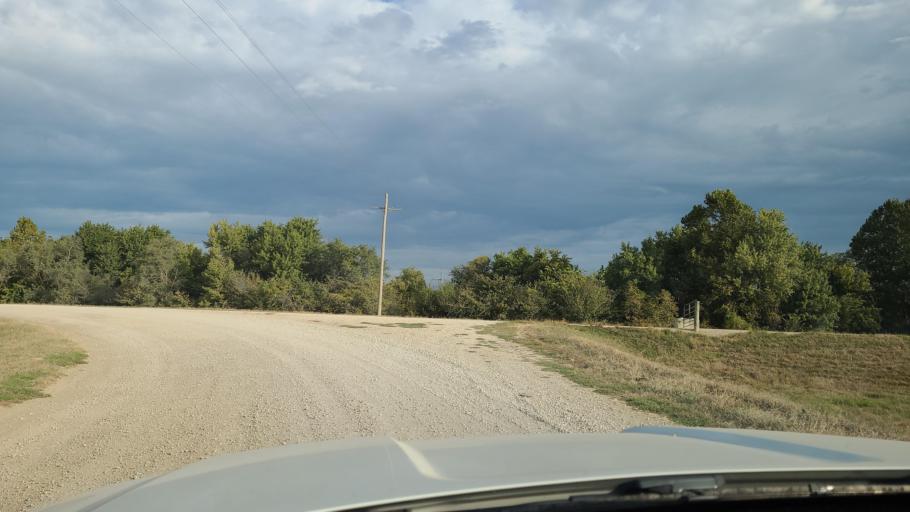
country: US
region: Kansas
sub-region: Douglas County
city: Lawrence
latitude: 39.0123
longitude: -95.2056
